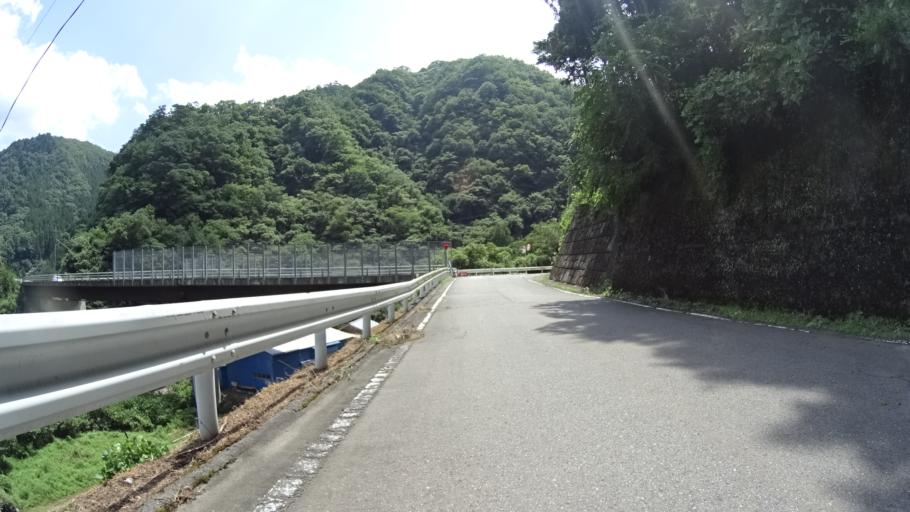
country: JP
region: Gunma
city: Tomioka
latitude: 36.0821
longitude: 138.7156
